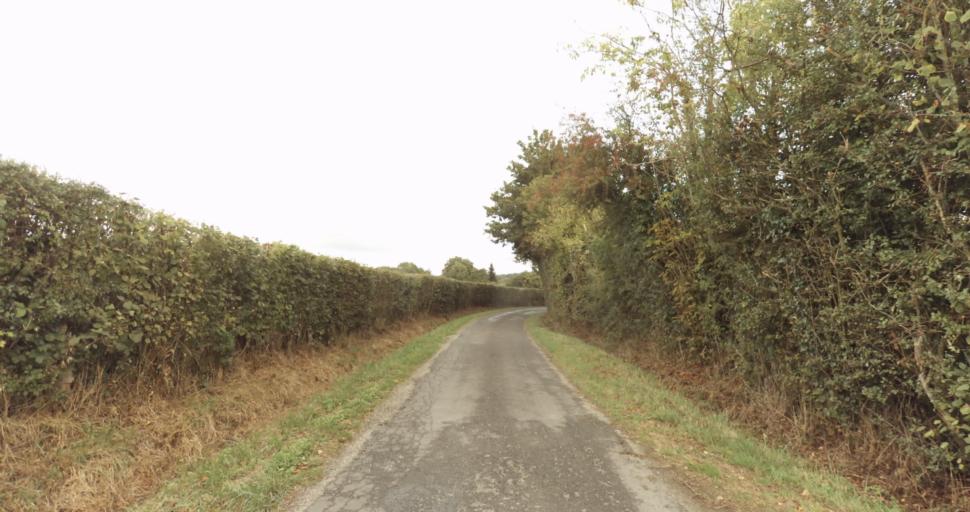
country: FR
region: Lower Normandy
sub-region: Departement de l'Orne
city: Sainte-Gauburge-Sainte-Colombe
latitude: 48.6975
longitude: 0.3649
